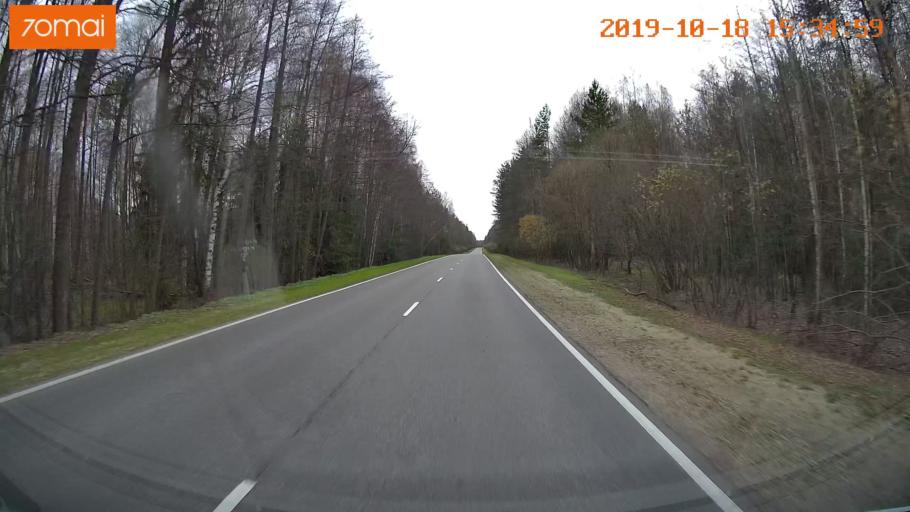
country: RU
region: Vladimir
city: Anopino
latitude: 55.8617
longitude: 40.6360
